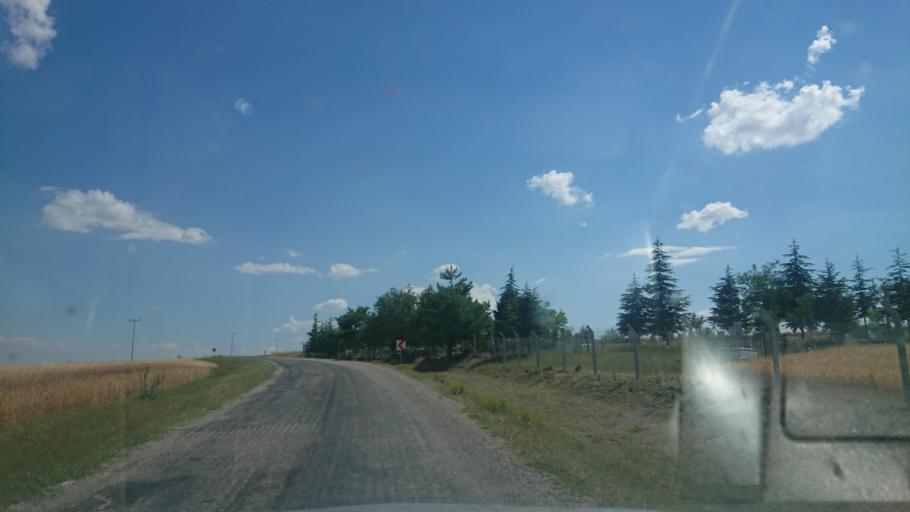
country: TR
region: Aksaray
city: Agacoren
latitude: 38.7638
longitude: 33.7829
